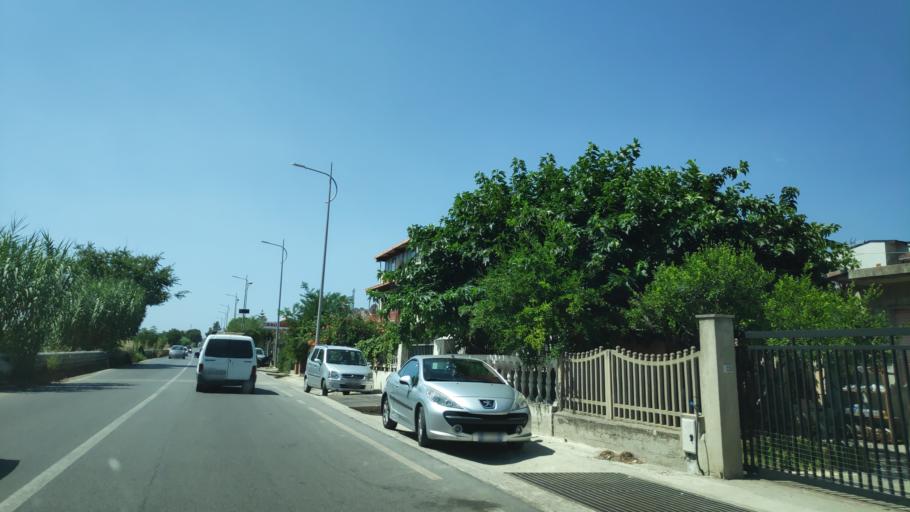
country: IT
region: Calabria
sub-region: Provincia di Reggio Calabria
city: Brancaleone-Marina
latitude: 37.9728
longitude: 16.1080
